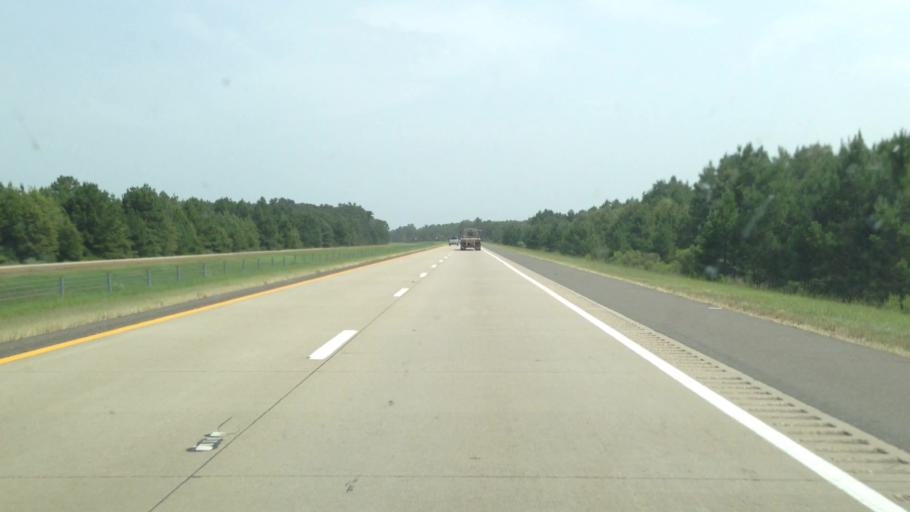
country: US
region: Texas
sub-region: Bowie County
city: Texarkana
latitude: 33.2050
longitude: -93.8760
